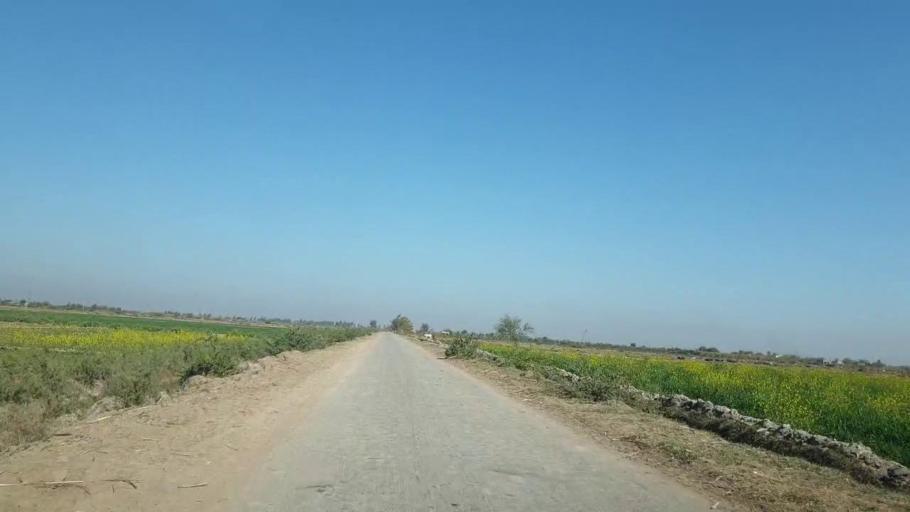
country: PK
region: Sindh
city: Mirpur Khas
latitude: 25.6000
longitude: 69.0450
